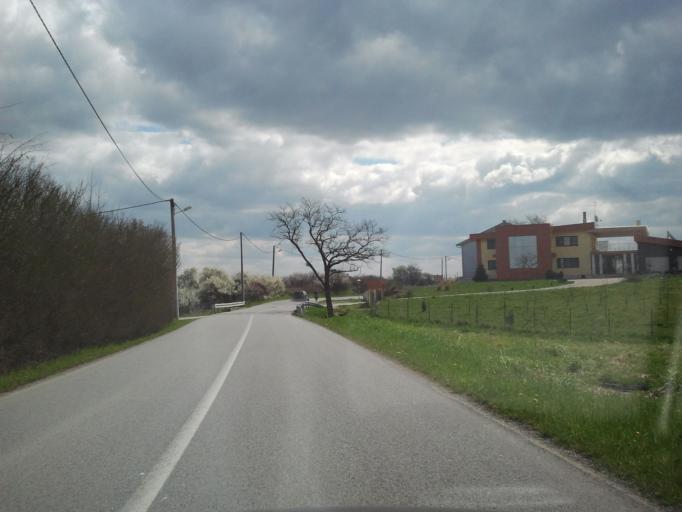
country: HR
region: Grad Zagreb
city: Brezovica
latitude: 45.7364
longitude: 15.8897
